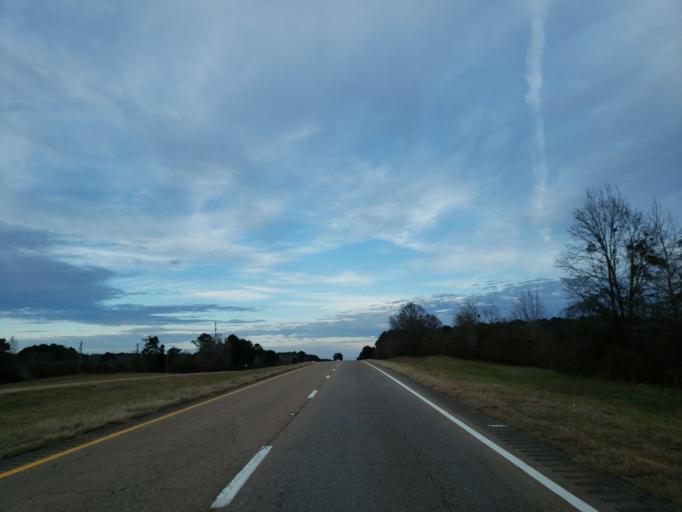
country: US
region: Mississippi
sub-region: Lauderdale County
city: Marion
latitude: 32.4707
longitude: -88.6105
